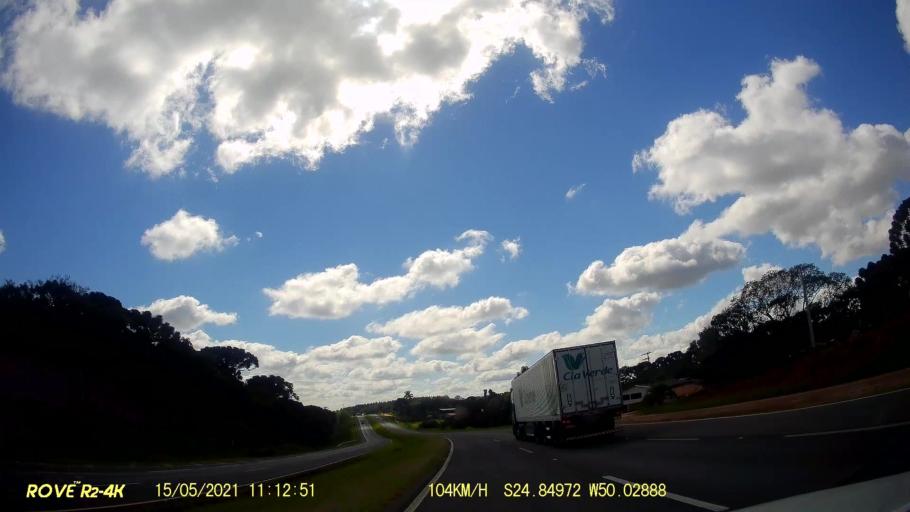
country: BR
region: Parana
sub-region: Castro
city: Castro
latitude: -24.8500
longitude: -50.0291
